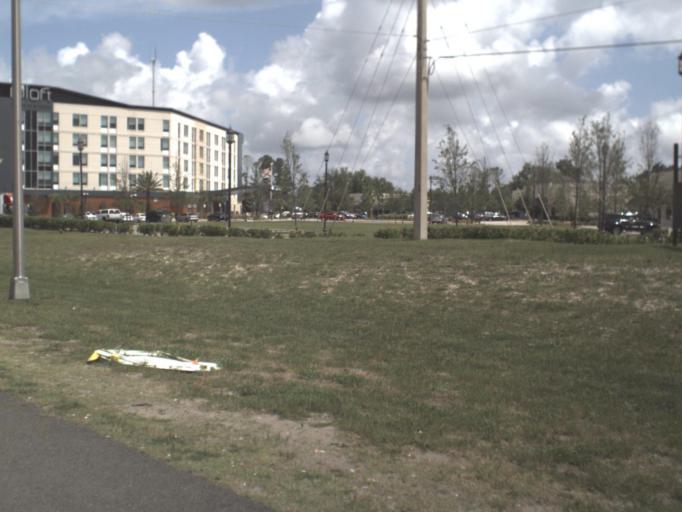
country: US
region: Florida
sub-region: Duval County
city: Jacksonville
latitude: 30.2582
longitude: -81.5551
